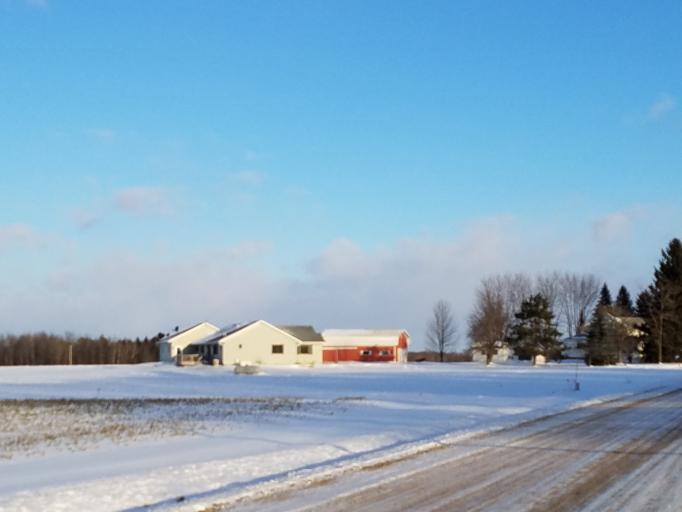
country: US
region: Wisconsin
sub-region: Clark County
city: Loyal
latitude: 44.6146
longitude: -90.4564
